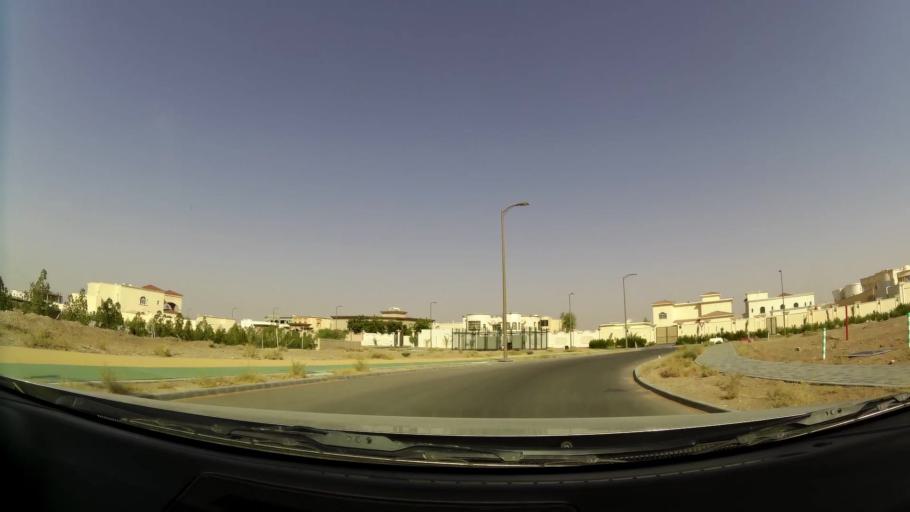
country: OM
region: Al Buraimi
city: Al Buraymi
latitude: 24.3604
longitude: 55.7932
